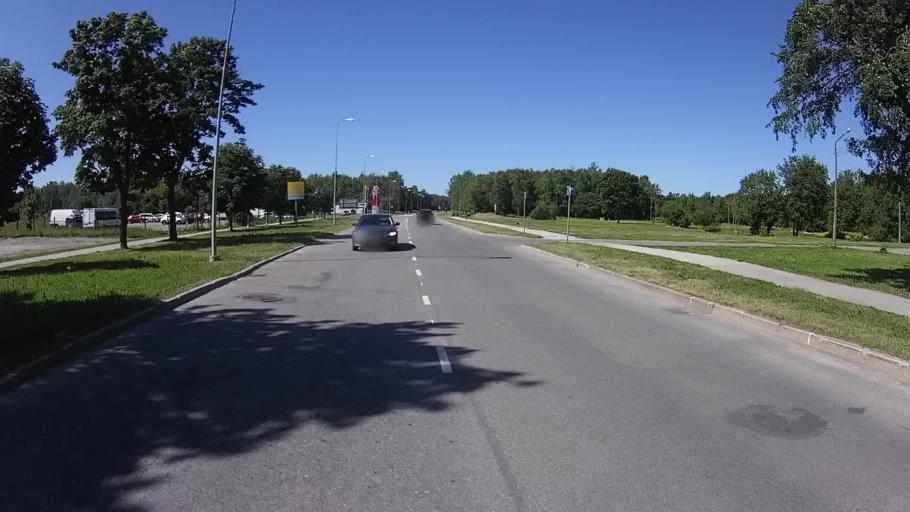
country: EE
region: Ida-Virumaa
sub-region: Kohtla-Jaerve linn
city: Kohtla-Jarve
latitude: 59.4089
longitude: 27.2800
